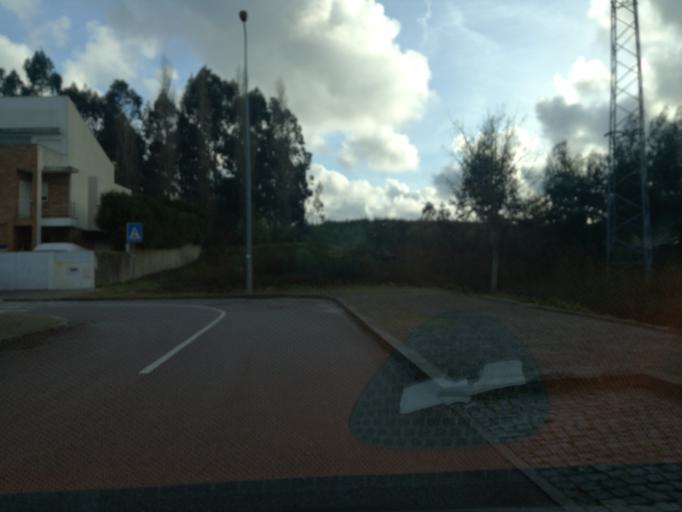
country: PT
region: Porto
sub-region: Maia
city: Nogueira
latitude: 41.2534
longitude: -8.5999
